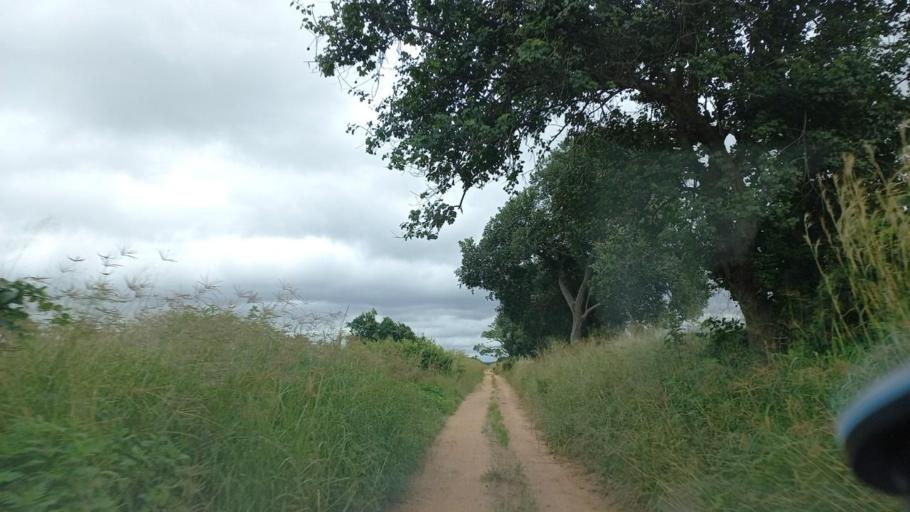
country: ZM
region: Lusaka
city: Lusaka
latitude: -15.1225
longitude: 28.3715
